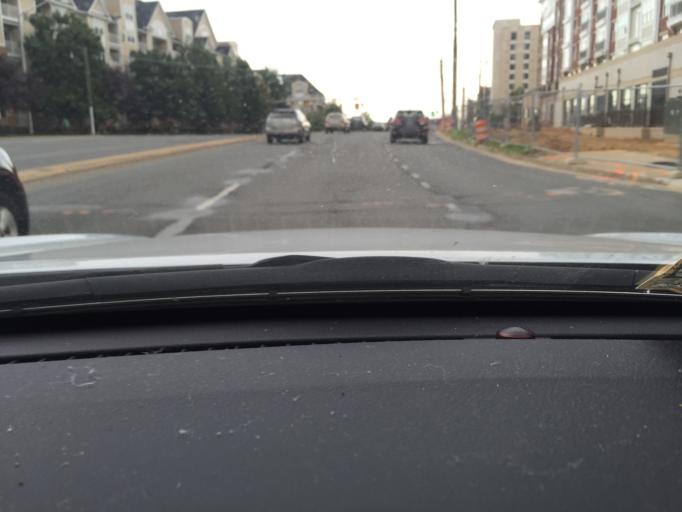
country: US
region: Virginia
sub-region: Fairfax County
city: Merrifield
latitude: 38.8819
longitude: -77.2277
